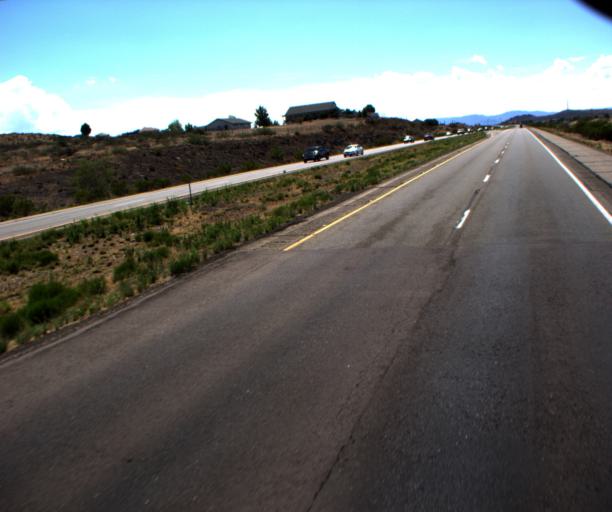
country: US
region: Arizona
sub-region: Yavapai County
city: Spring Valley
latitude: 34.3601
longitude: -112.1719
